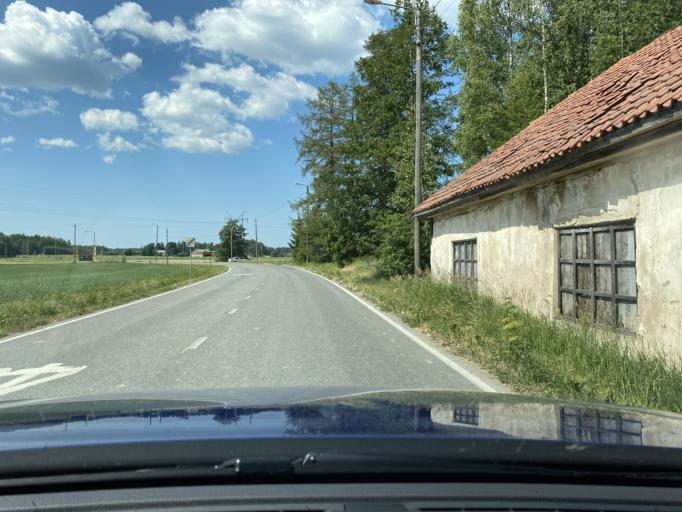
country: FI
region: Satakunta
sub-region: Rauma
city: Eura
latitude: 61.1450
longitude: 22.1123
